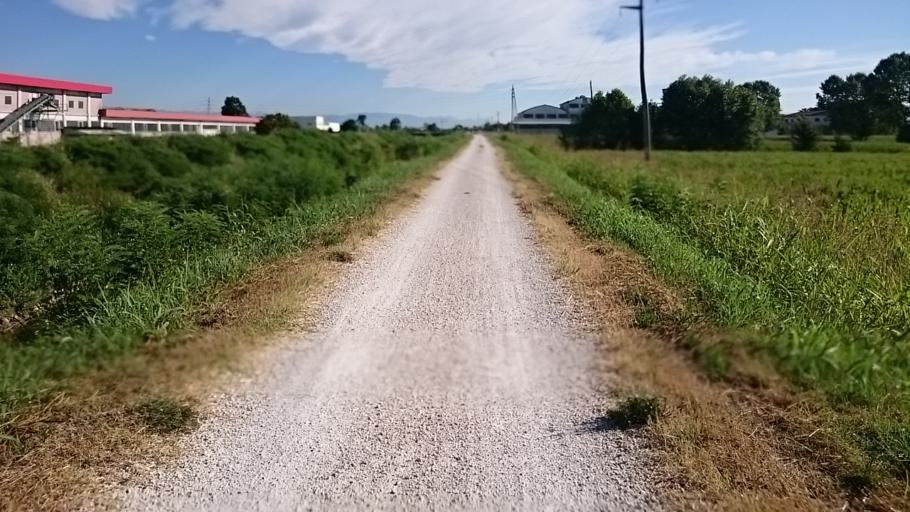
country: IT
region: Veneto
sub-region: Provincia di Padova
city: Borgoricco-San Michele delle Badesse-Sant'Eufemia
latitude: 45.5354
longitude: 11.9249
